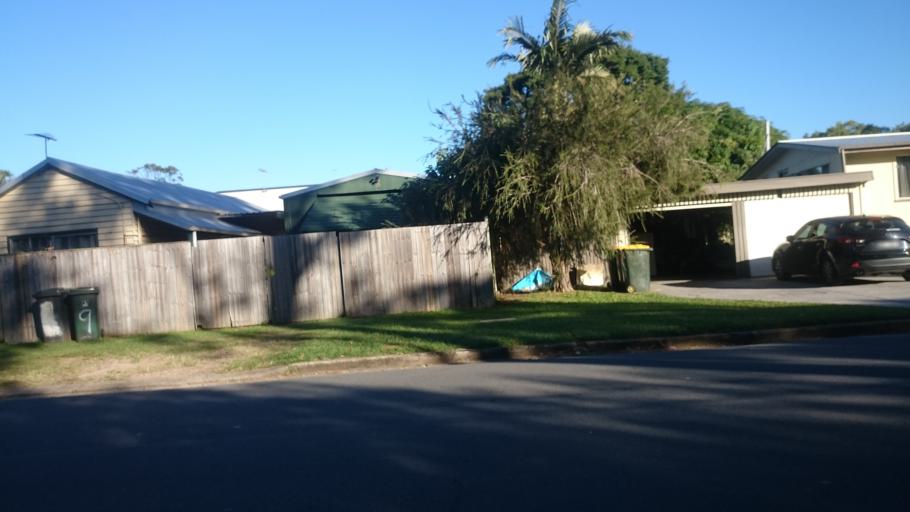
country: AU
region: Queensland
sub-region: Brisbane
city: Manly West
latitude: -27.4683
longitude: 153.1883
